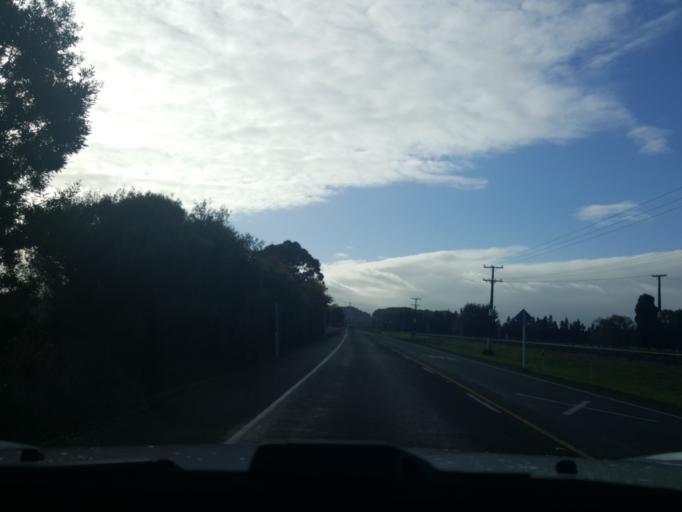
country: NZ
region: Waikato
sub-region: Waipa District
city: Cambridge
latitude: -37.6680
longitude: 175.4854
